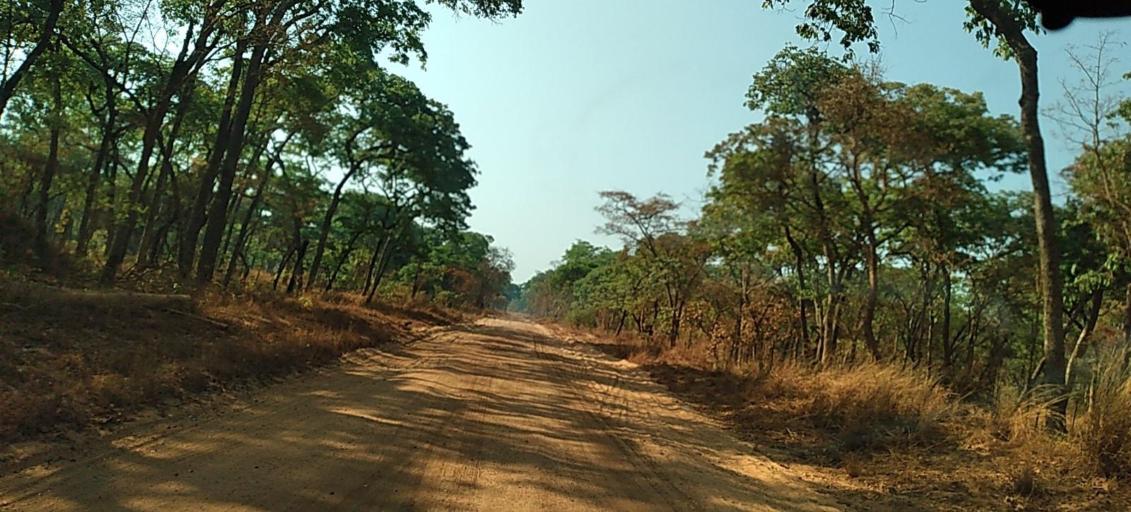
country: ZM
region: North-Western
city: Kasempa
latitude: -13.6452
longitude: 26.0000
